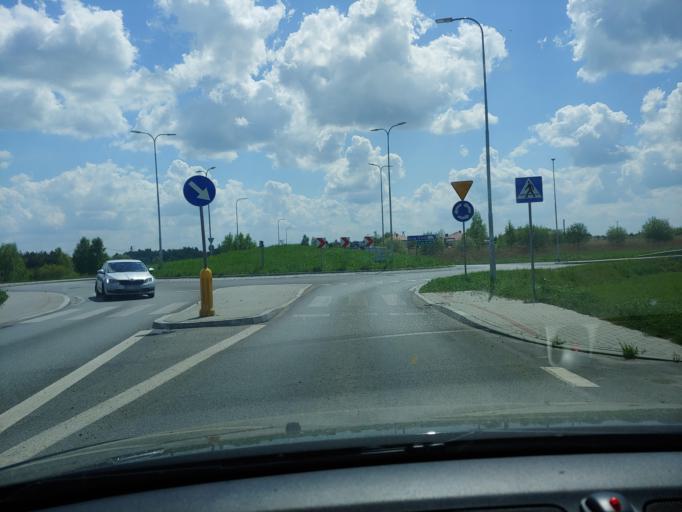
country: PL
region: Subcarpathian Voivodeship
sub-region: Powiat mielecki
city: Radomysl Wielki
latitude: 50.2079
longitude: 21.2798
